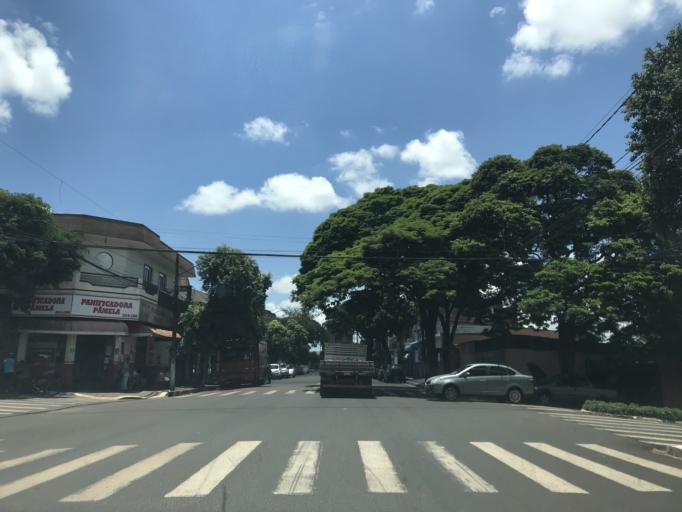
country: BR
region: Parana
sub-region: Marialva
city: Marialva
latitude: -23.4886
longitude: -51.7930
